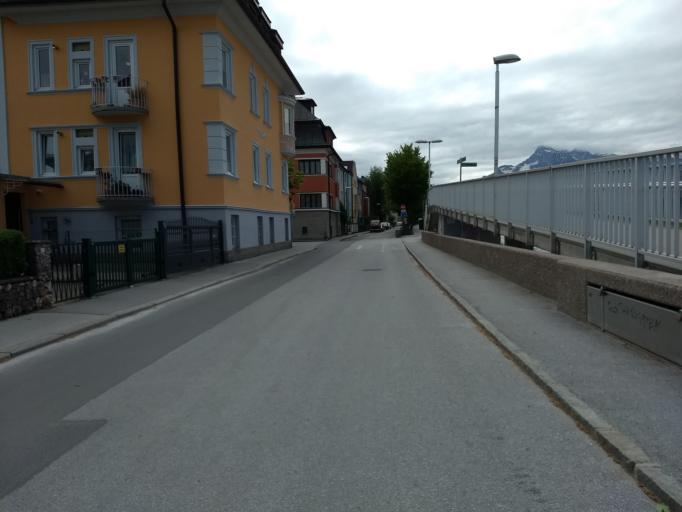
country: AT
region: Salzburg
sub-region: Salzburg Stadt
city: Salzburg
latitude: 47.8146
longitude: 13.0374
